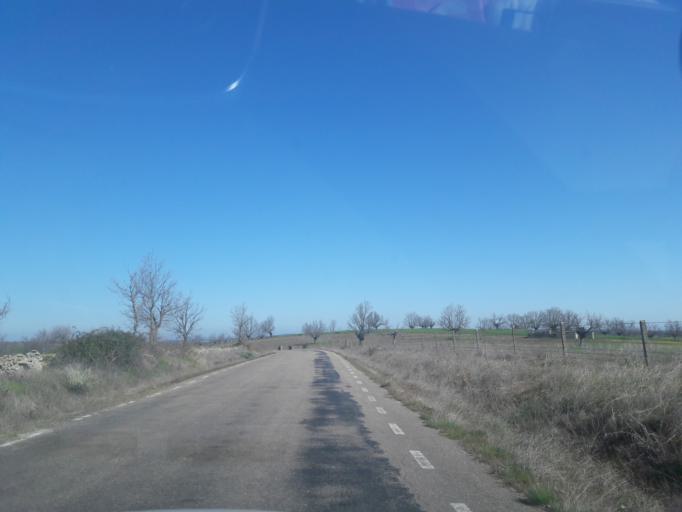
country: ES
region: Castille and Leon
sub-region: Provincia de Salamanca
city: Valsalabroso
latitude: 41.1373
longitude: -6.4831
